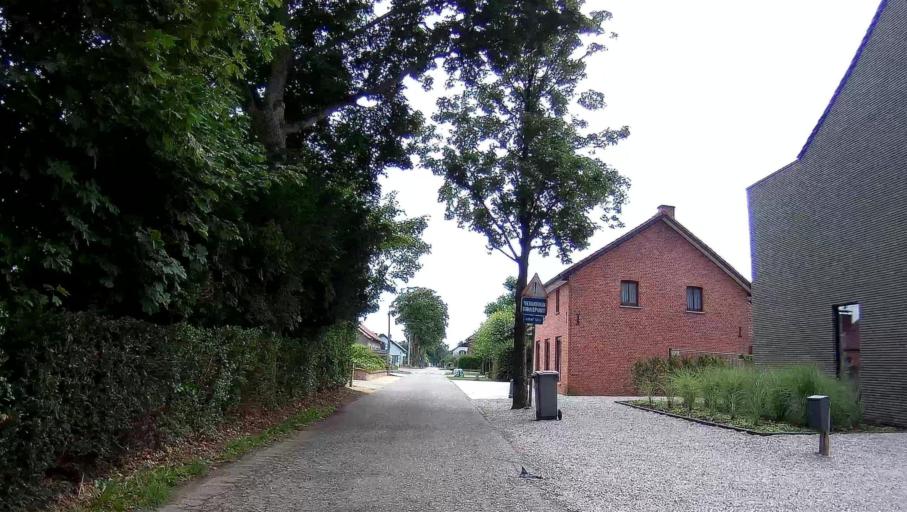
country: BE
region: Flanders
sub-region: Provincie Antwerpen
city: Balen
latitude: 51.1934
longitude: 5.2154
